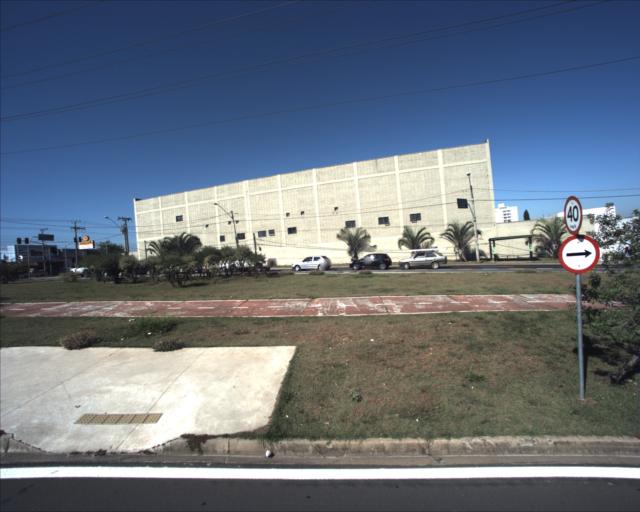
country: BR
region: Sao Paulo
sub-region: Sorocaba
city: Sorocaba
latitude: -23.5149
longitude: -47.4899
